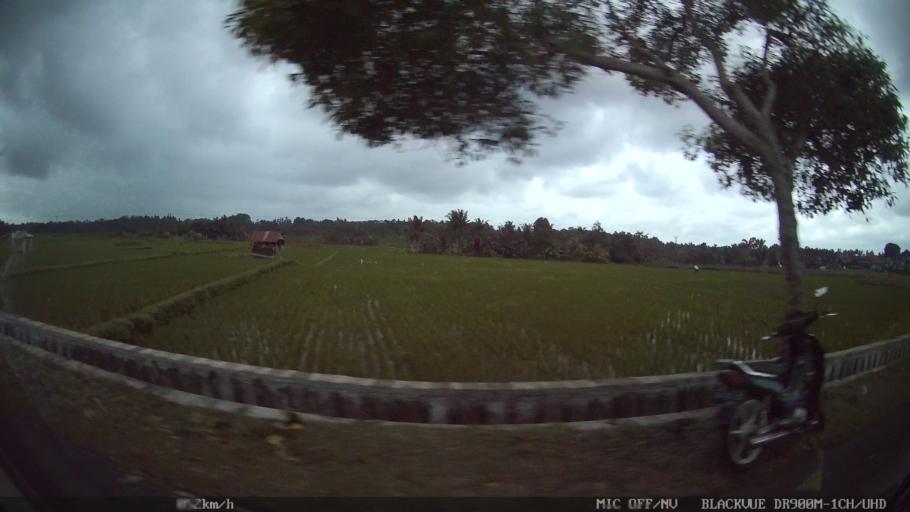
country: ID
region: Bali
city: Banjar Sempidi
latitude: -8.5205
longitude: 115.1953
